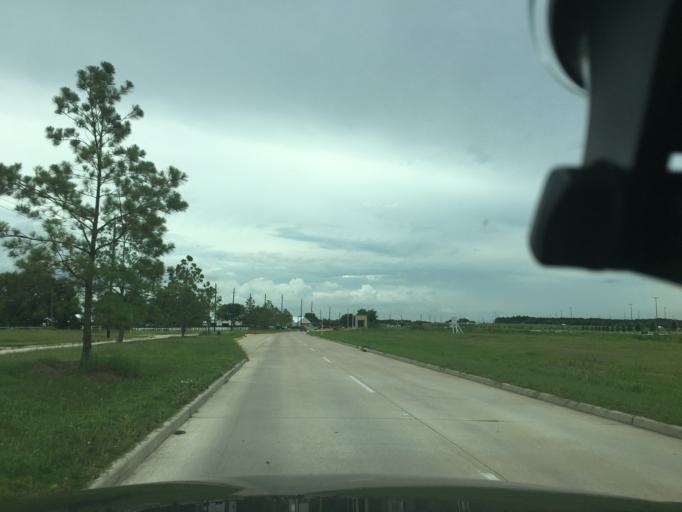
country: US
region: Texas
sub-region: Harris County
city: Tomball
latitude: 30.0603
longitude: -95.6983
